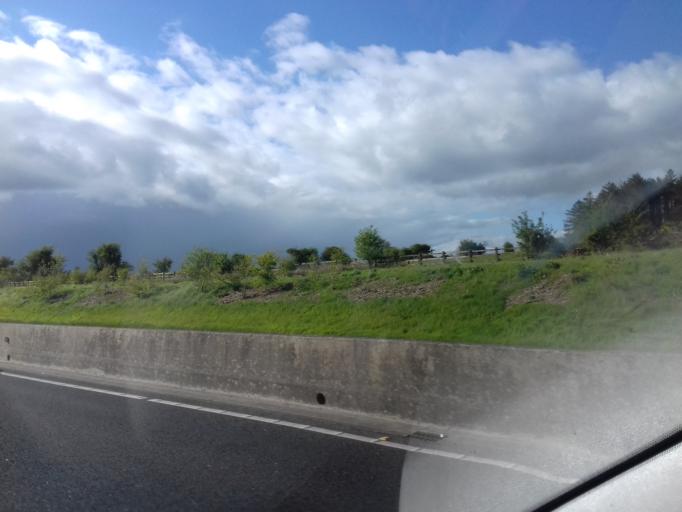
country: IE
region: Leinster
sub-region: Kilkenny
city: Mooncoin
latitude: 52.4065
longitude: -7.2019
